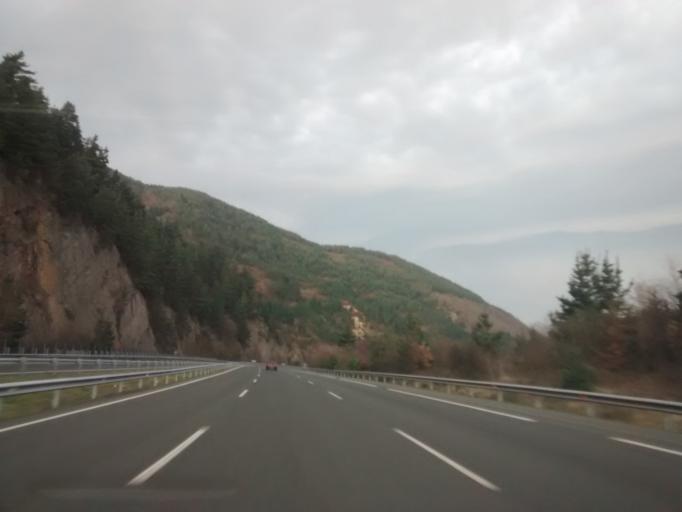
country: ES
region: Basque Country
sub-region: Provincia de Alava
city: Lezama
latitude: 43.0619
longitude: -2.9310
